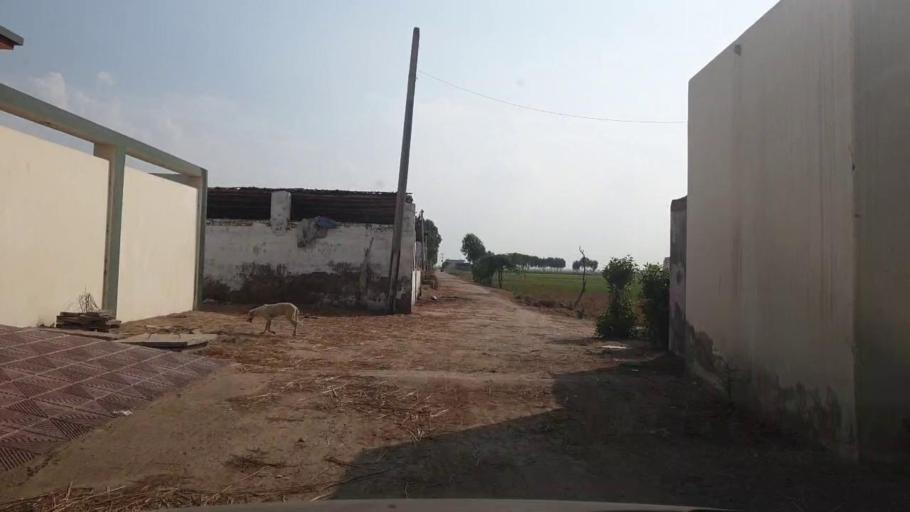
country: PK
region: Sindh
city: Kario
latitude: 24.6376
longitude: 68.5580
